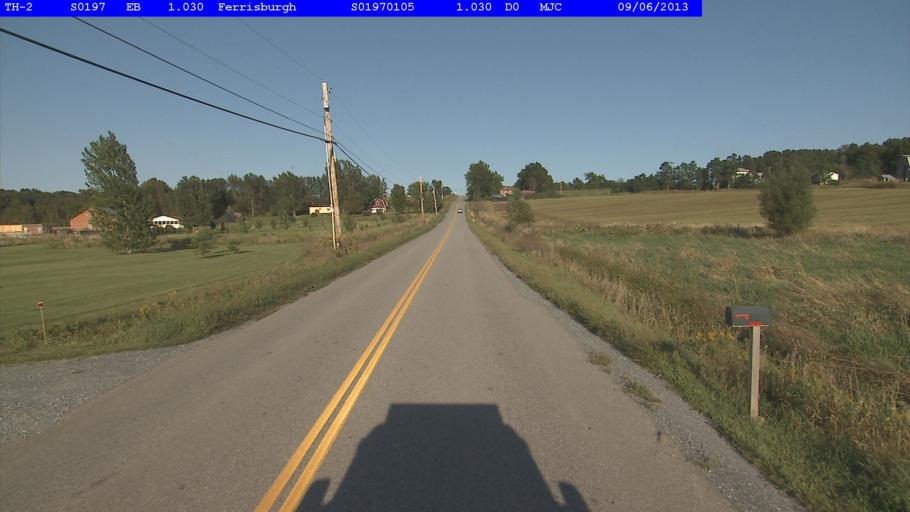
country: US
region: Vermont
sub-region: Addison County
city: Vergennes
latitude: 44.1743
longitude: -73.2190
